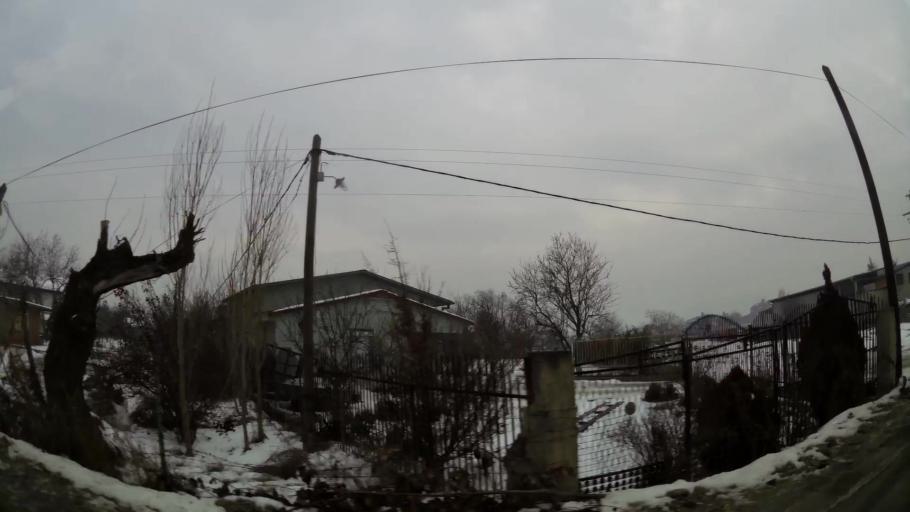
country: MK
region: Cucer-Sandevo
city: Chucher - Sandevo
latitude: 42.0479
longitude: 21.3659
